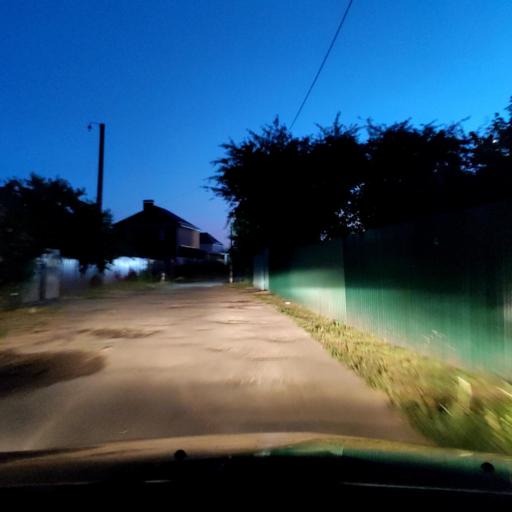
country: RU
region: Voronezj
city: Podgornoye
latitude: 51.8000
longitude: 39.2200
